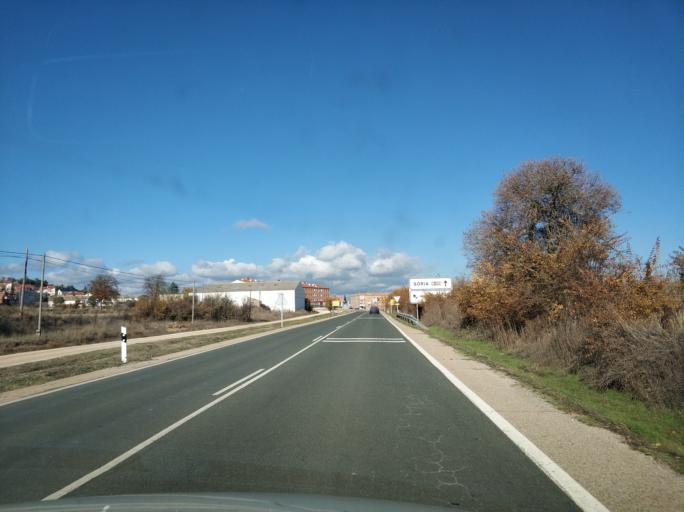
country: ES
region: Castille and Leon
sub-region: Provincia de Soria
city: Almazan
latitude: 41.4775
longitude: -2.5296
